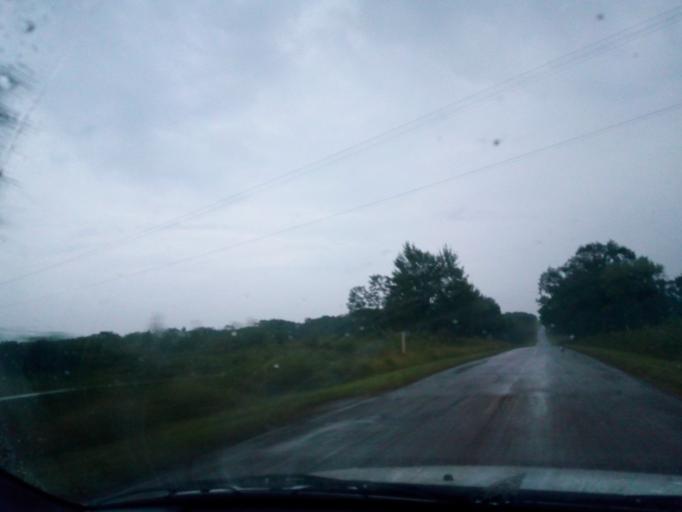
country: RU
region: Primorskiy
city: Lazo
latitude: 45.8701
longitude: 133.6966
